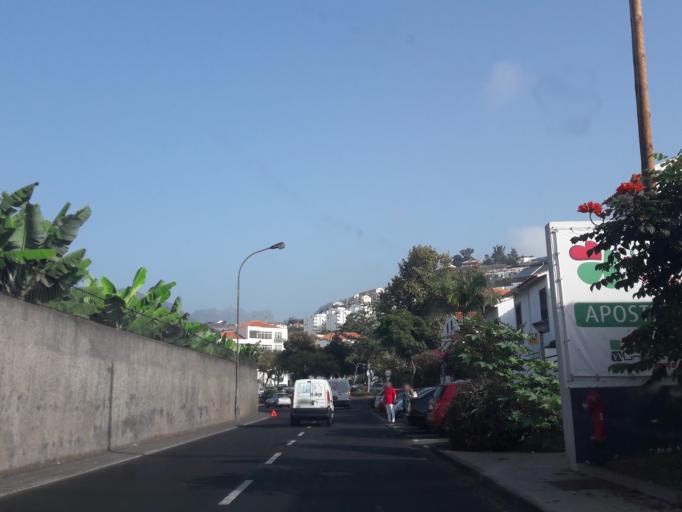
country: PT
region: Madeira
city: Camara de Lobos
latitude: 32.6569
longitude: -16.9463
